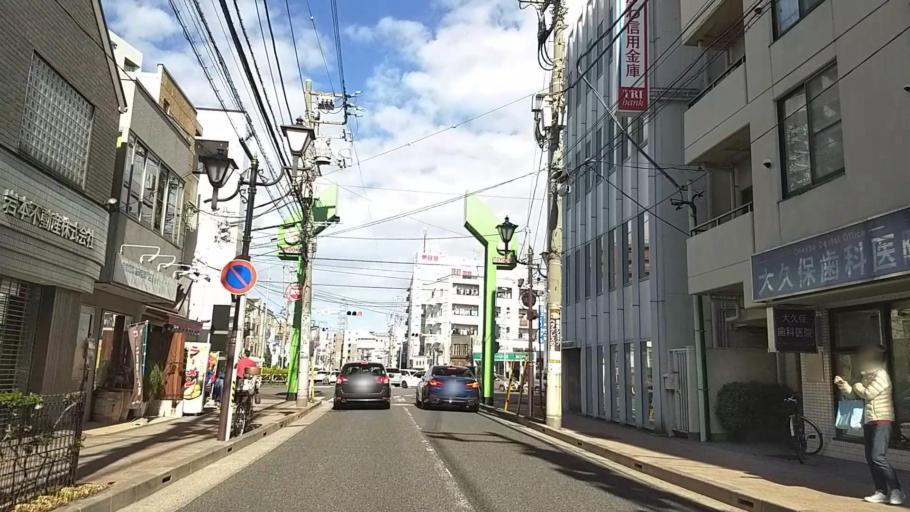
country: JP
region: Kanagawa
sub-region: Kawasaki-shi
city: Kawasaki
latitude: 35.5130
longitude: 139.6745
